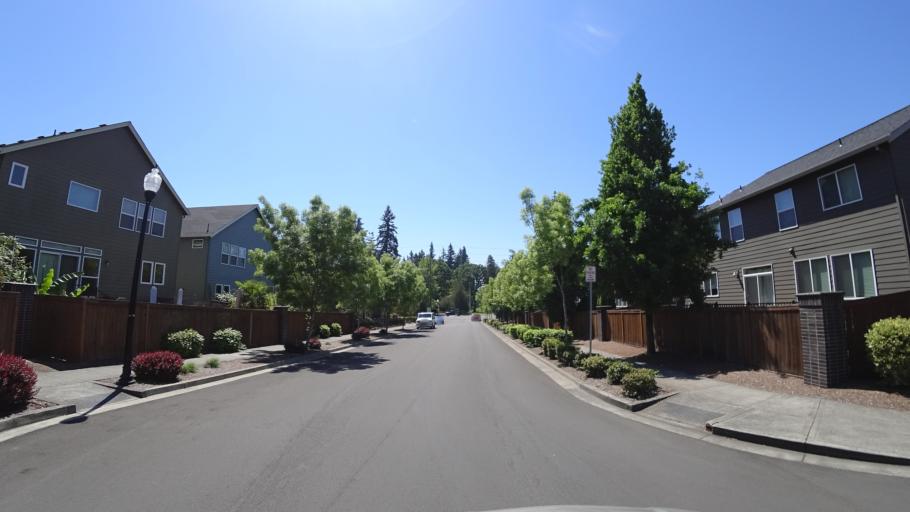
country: US
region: Oregon
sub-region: Washington County
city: Rockcreek
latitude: 45.5209
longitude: -122.9260
